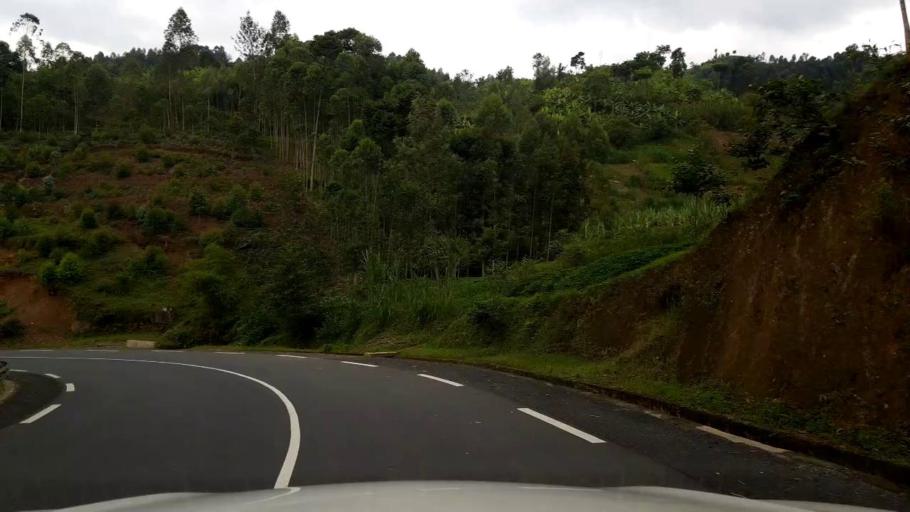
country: RW
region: Western Province
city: Kibuye
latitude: -1.9061
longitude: 29.3627
